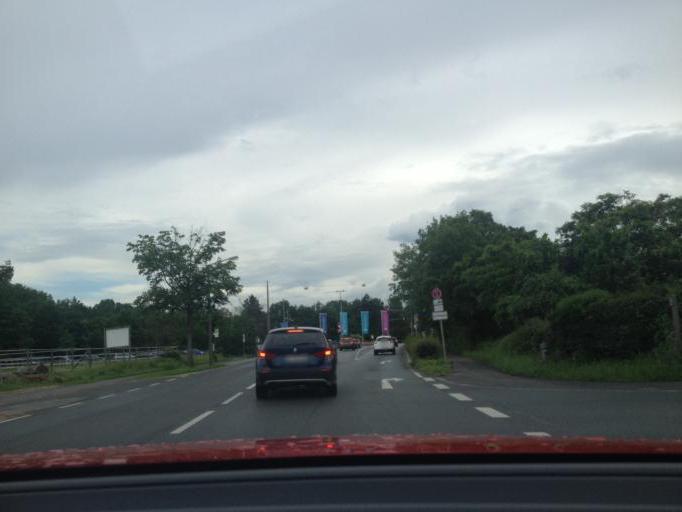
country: DE
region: Bavaria
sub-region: Regierungsbezirk Mittelfranken
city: Nuernberg
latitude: 49.4857
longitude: 11.0823
